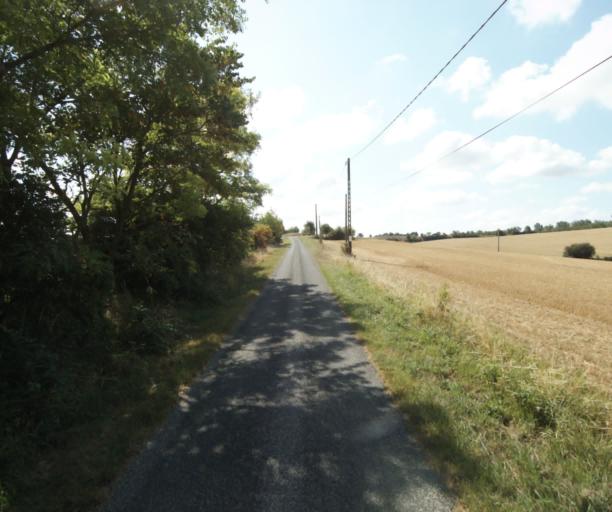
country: FR
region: Midi-Pyrenees
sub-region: Departement de la Haute-Garonne
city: Avignonet-Lauragais
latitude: 43.4377
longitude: 1.7889
